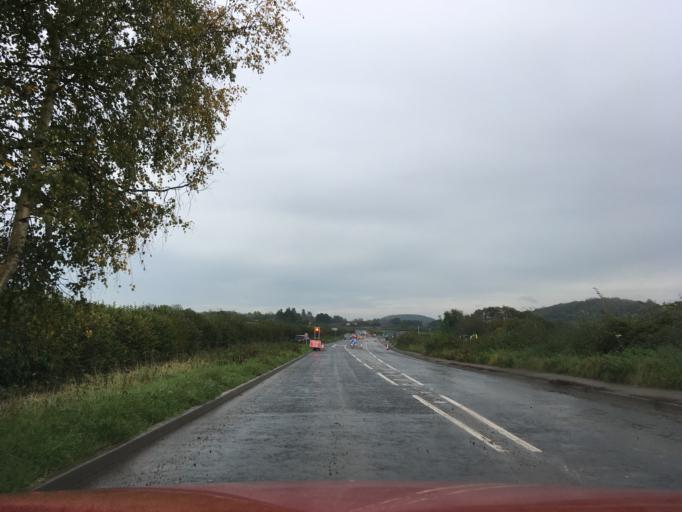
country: GB
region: Wales
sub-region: Newport
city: Bishton
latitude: 51.6044
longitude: -2.8864
